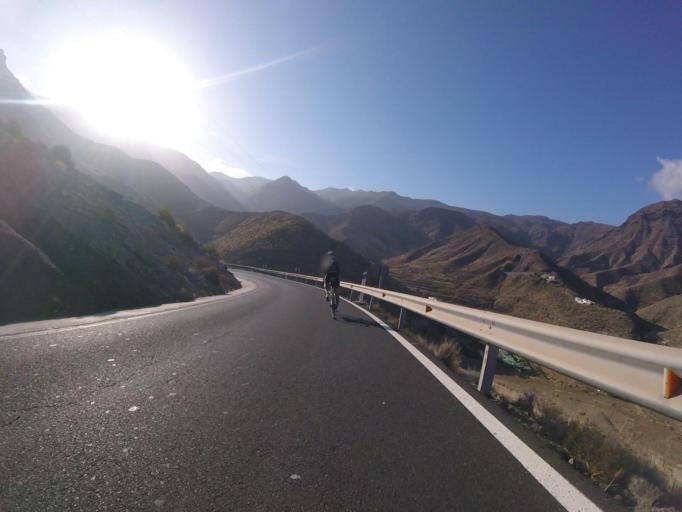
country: ES
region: Canary Islands
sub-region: Provincia de Las Palmas
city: Agaete
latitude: 28.0531
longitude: -15.7331
